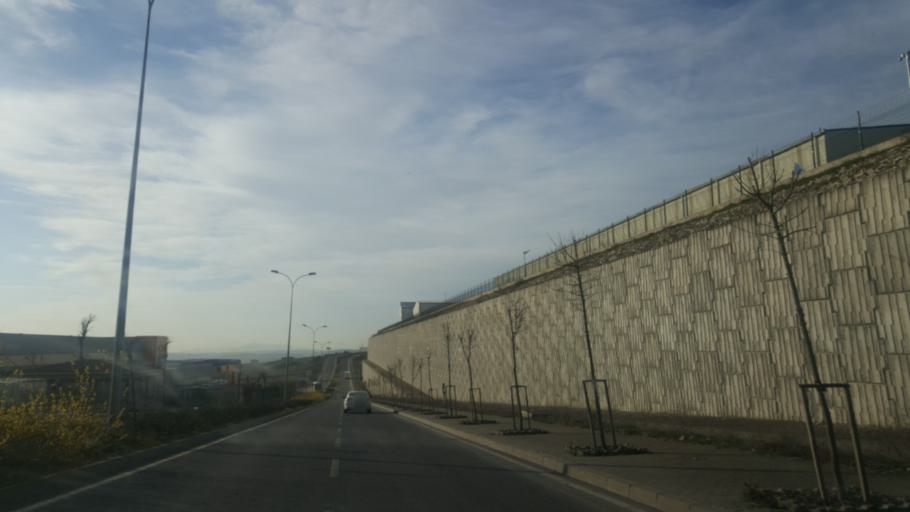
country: TR
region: Kocaeli
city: Tavsanli
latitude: 40.8314
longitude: 29.5569
